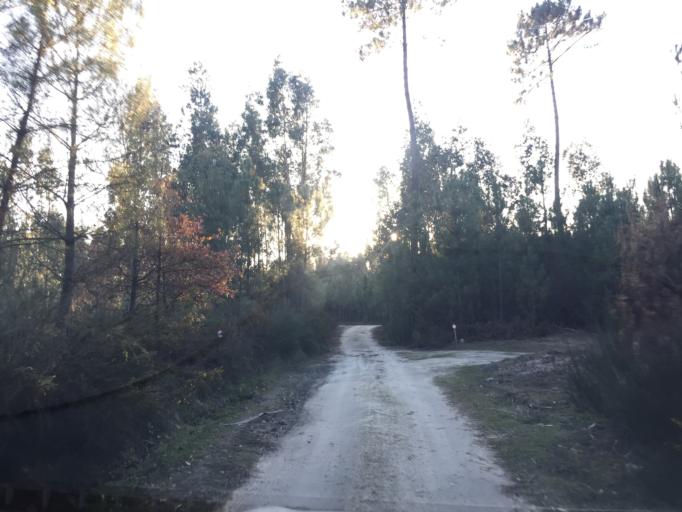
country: PT
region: Viseu
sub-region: Concelho de Carregal do Sal
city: Carregal do Sal
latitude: 40.4622
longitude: -7.9304
